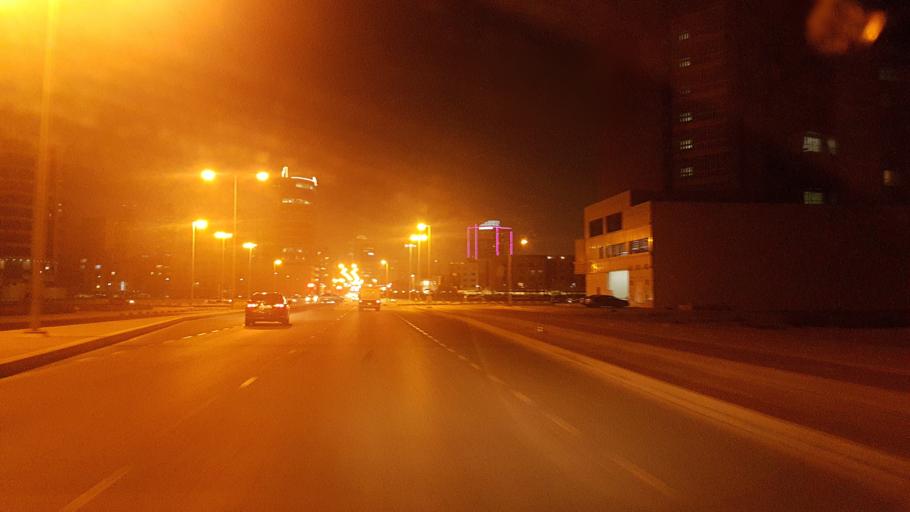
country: BH
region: Manama
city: Jidd Hafs
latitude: 26.2367
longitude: 50.5276
